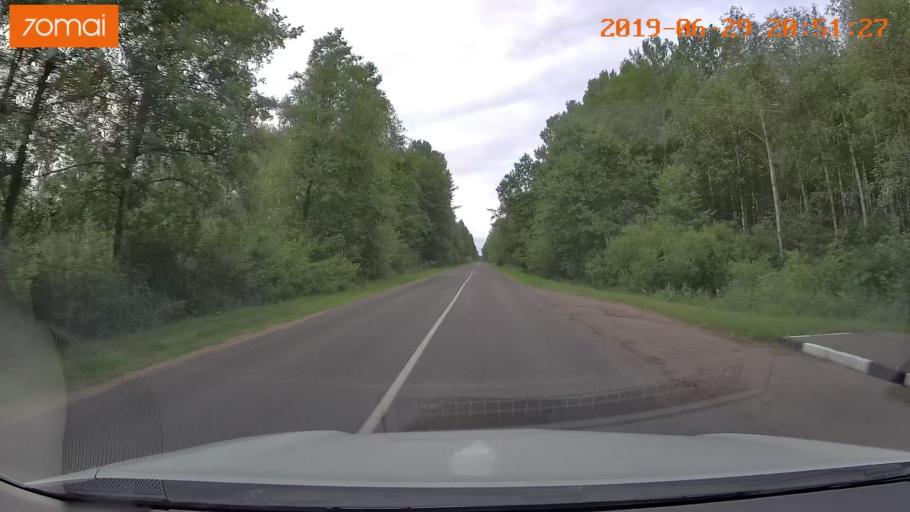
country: BY
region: Brest
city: Hantsavichy
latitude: 52.6882
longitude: 26.3497
